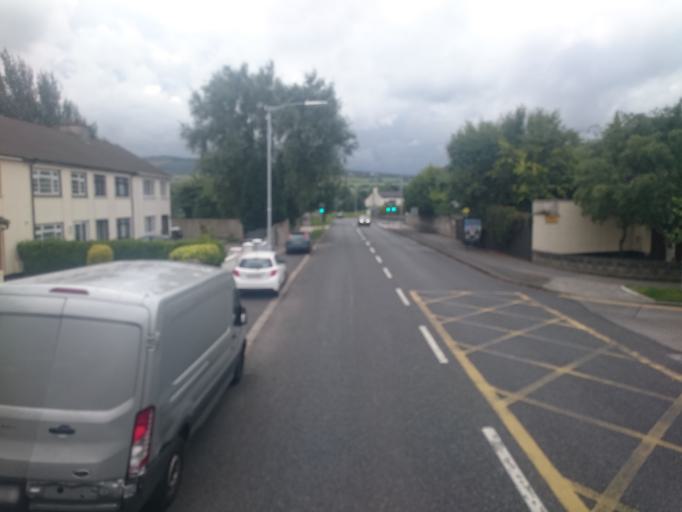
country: IE
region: Leinster
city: Oldbawn
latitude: 53.2792
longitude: -6.3584
